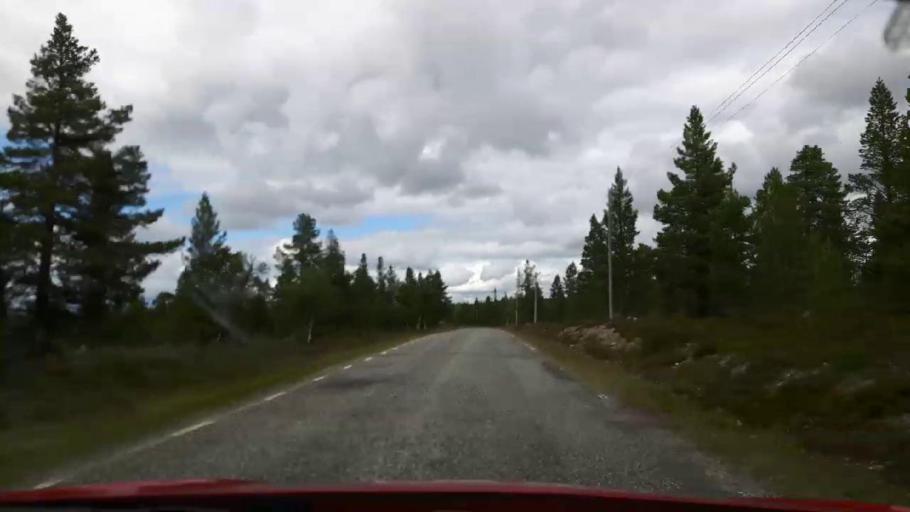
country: NO
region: Hedmark
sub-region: Engerdal
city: Engerdal
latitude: 62.3223
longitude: 12.8089
